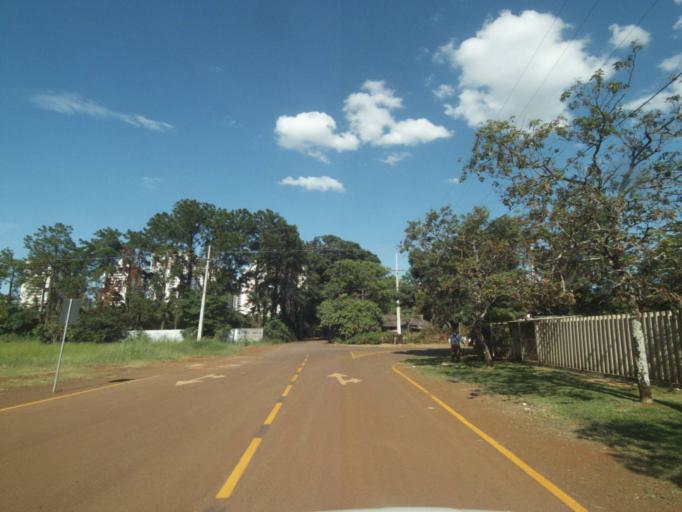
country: BR
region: Parana
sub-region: Londrina
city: Londrina
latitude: -23.3349
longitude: -51.1865
